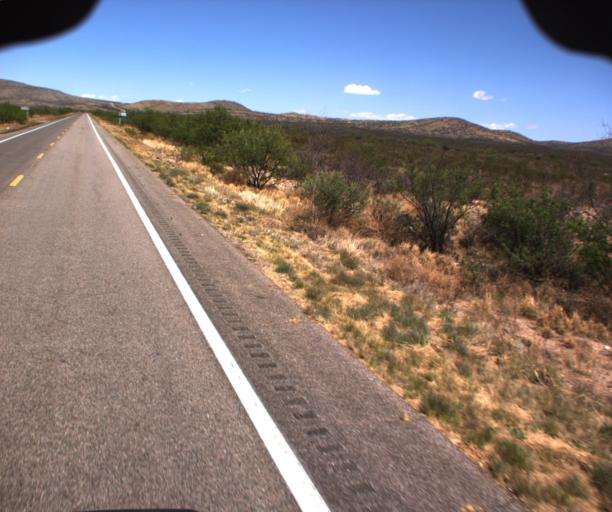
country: US
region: Arizona
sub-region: Cochise County
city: Tombstone
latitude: 31.6320
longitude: -110.0459
